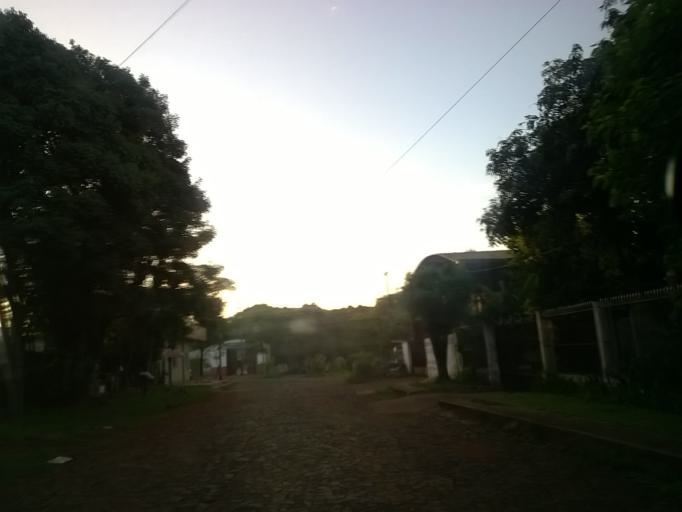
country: PY
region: Alto Parana
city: Ciudad del Este
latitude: -25.5054
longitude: -54.6534
